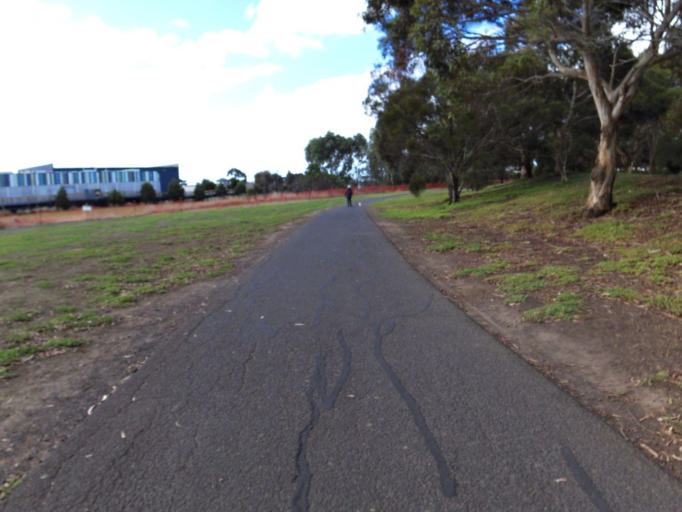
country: AU
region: Victoria
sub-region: Greater Geelong
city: Wandana Heights
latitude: -38.2049
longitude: 144.3102
